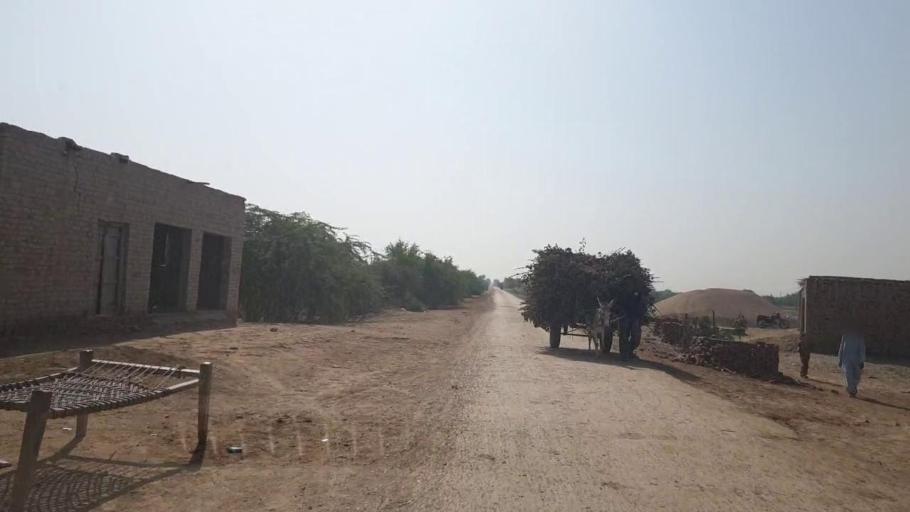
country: PK
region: Sindh
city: Shahdadpur
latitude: 25.9065
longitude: 68.7438
